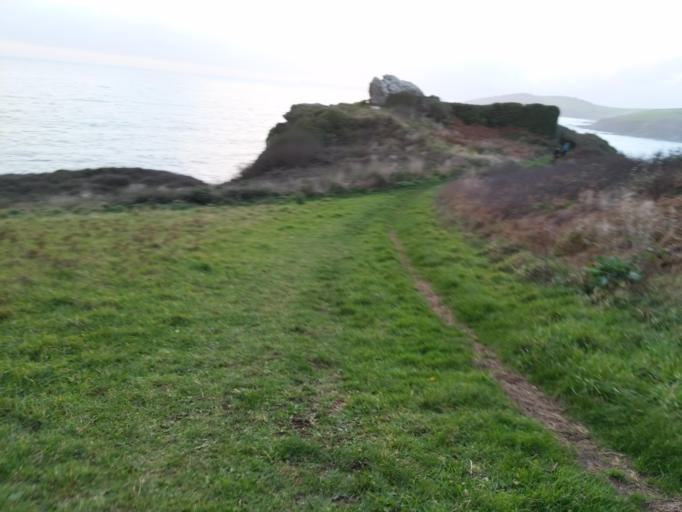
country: GB
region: England
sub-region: Cornwall
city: Fowey
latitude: 50.3267
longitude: -4.6374
